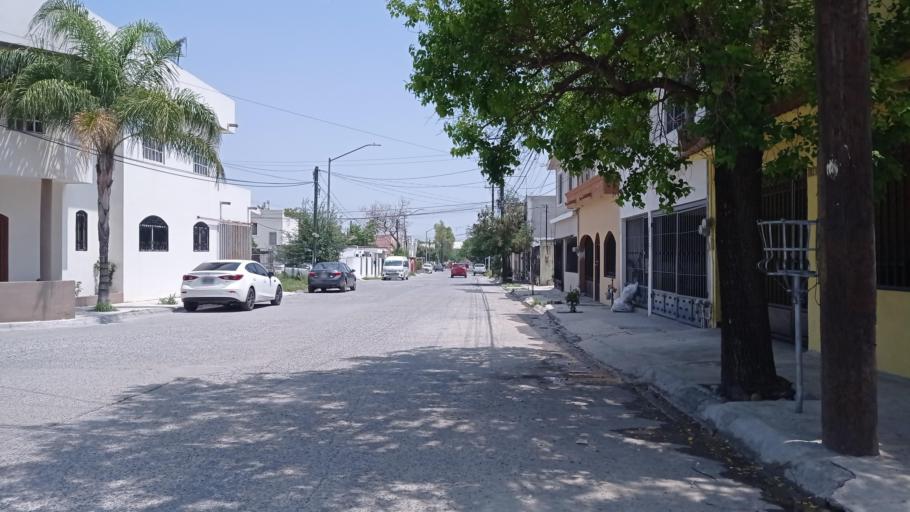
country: MX
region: Nuevo Leon
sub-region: Juarez
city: Jardines de la Silla (Jardines)
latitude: 25.6521
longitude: -100.1913
